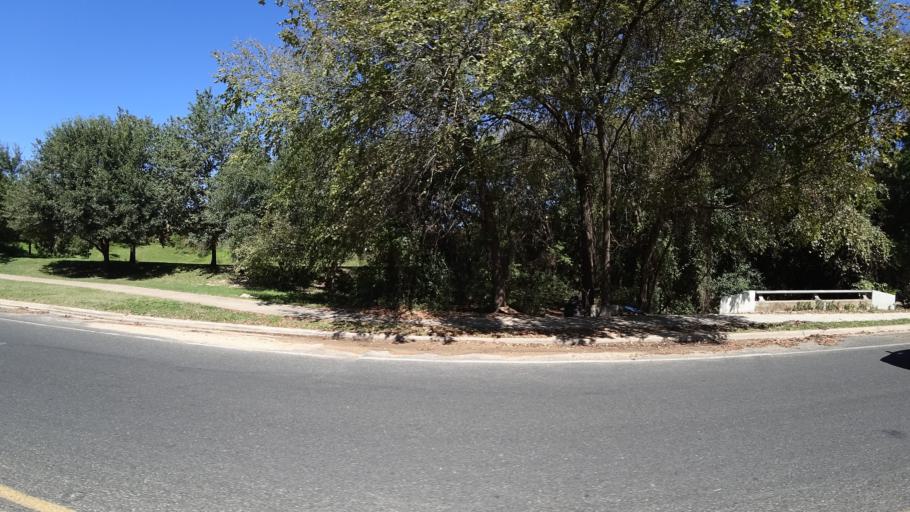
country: US
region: Texas
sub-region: Travis County
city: Austin
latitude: 30.2254
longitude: -97.7514
